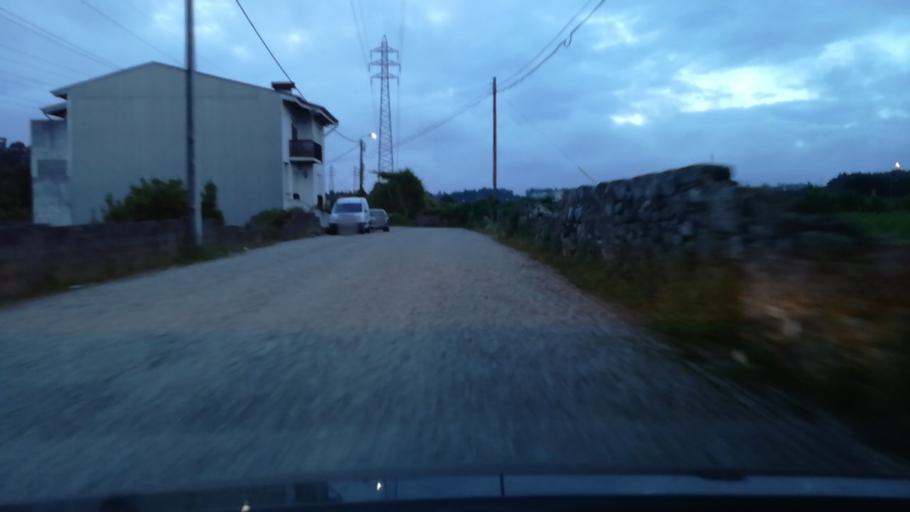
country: PT
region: Porto
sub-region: Maia
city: Anta
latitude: 41.2524
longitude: -8.6204
